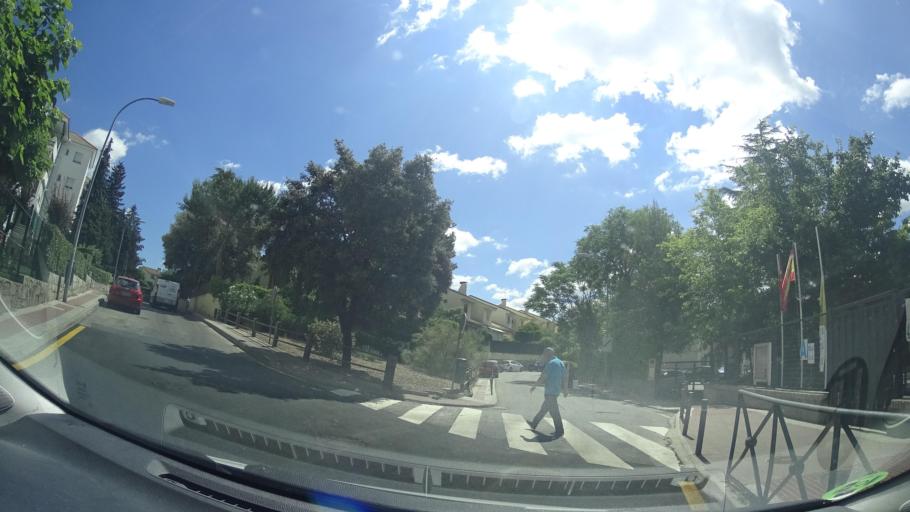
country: ES
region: Madrid
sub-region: Provincia de Madrid
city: Collado-Villalba
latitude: 40.6270
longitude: -4.0010
